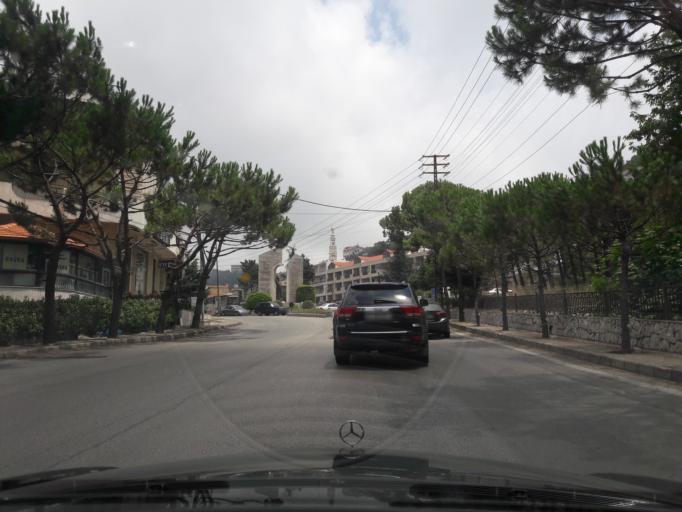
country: LB
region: Mont-Liban
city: Djounie
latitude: 33.9178
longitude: 35.6740
